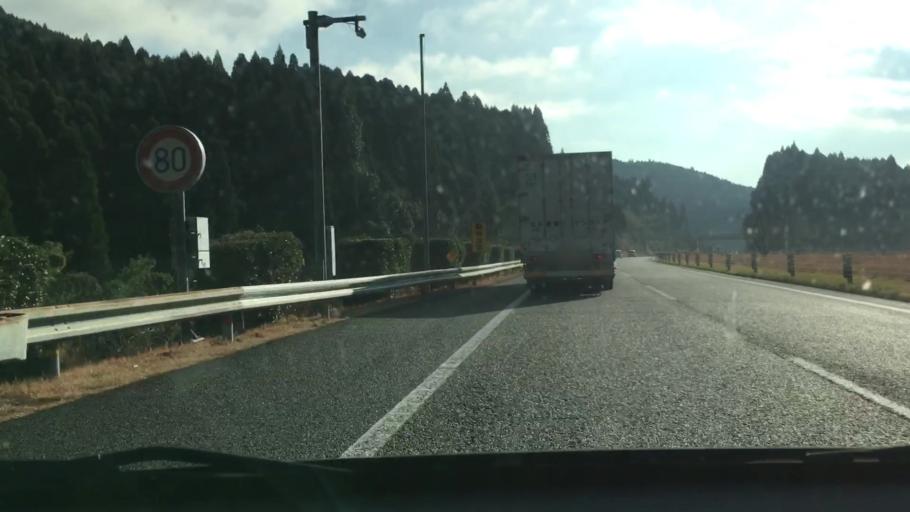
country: JP
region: Kagoshima
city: Okuchi-shinohara
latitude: 31.9647
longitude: 130.7461
